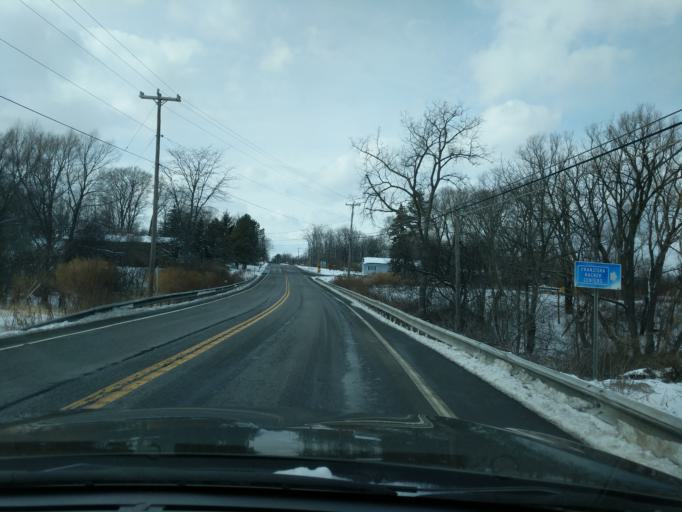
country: US
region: New York
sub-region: Tompkins County
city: Northwest Ithaca
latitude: 42.4852
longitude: -76.5707
